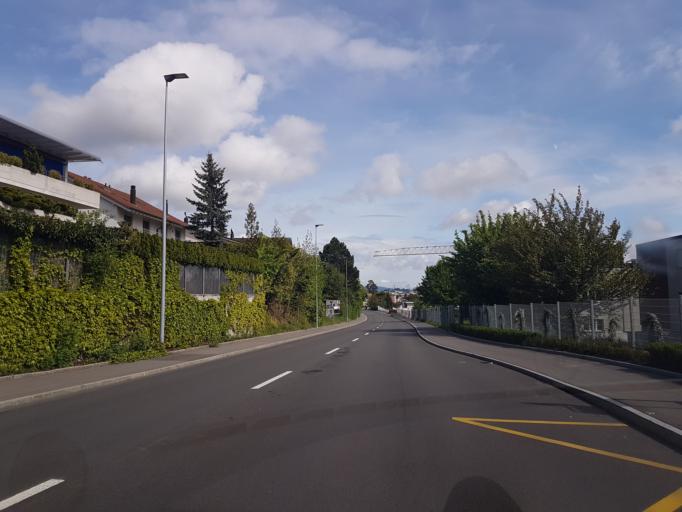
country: CH
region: Zurich
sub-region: Bezirk Dietikon
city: Geroldswil
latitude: 47.4234
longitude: 8.4036
